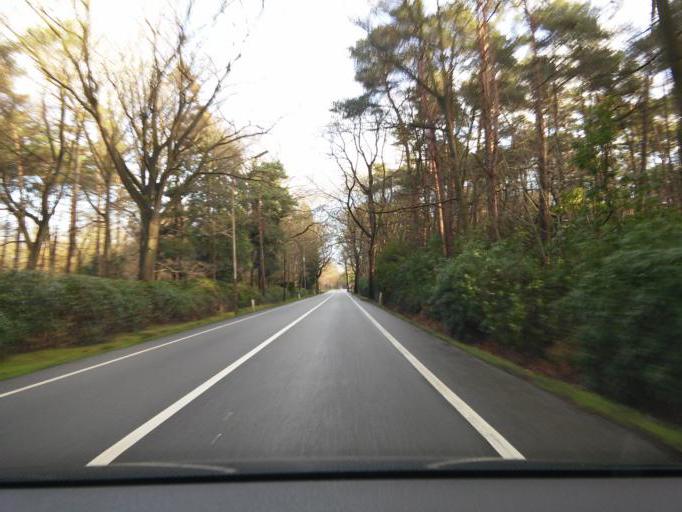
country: BE
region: Flanders
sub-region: Provincie Antwerpen
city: Kapellen
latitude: 51.3599
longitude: 4.4287
